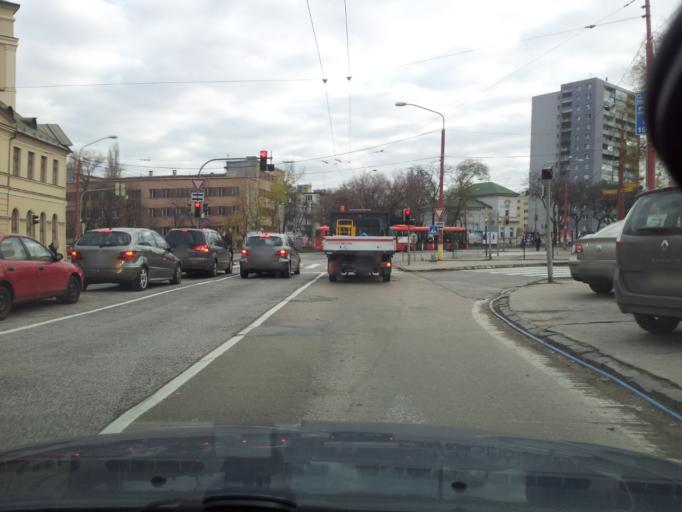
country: SK
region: Bratislavsky
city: Bratislava
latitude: 48.1560
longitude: 17.1242
